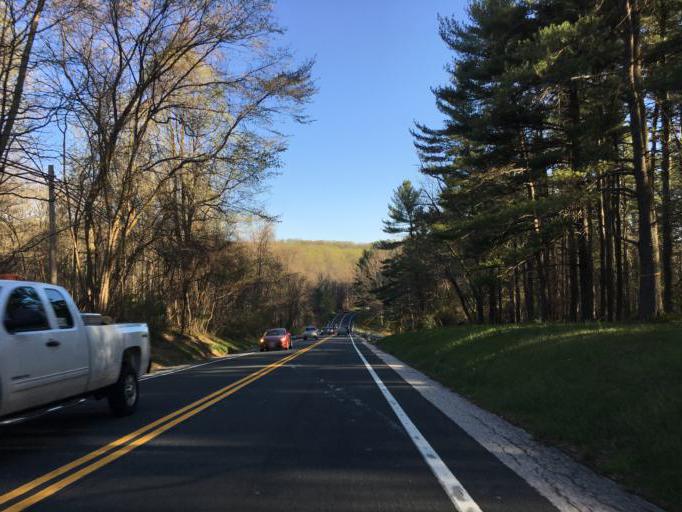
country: US
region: Maryland
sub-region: Baltimore County
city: Hampton
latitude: 39.4522
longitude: -76.5925
